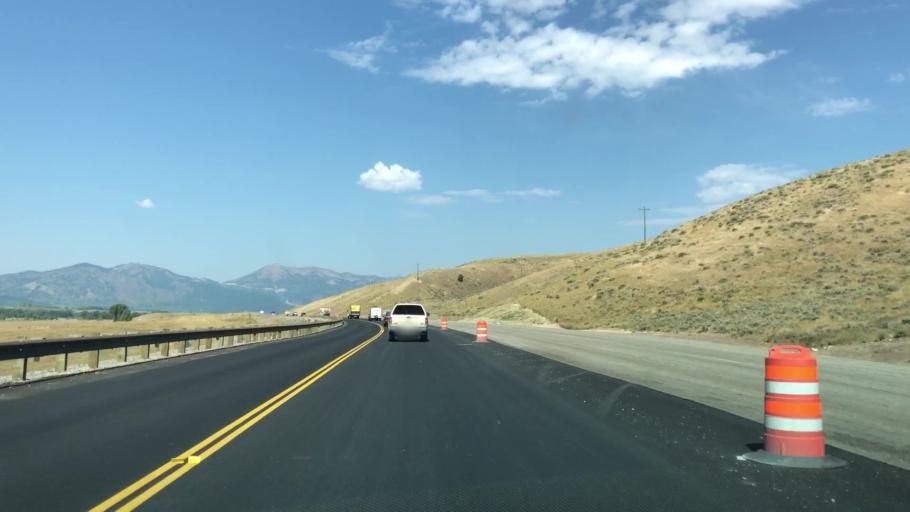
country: US
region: Wyoming
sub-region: Teton County
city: South Park
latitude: 43.4044
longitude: -110.7582
